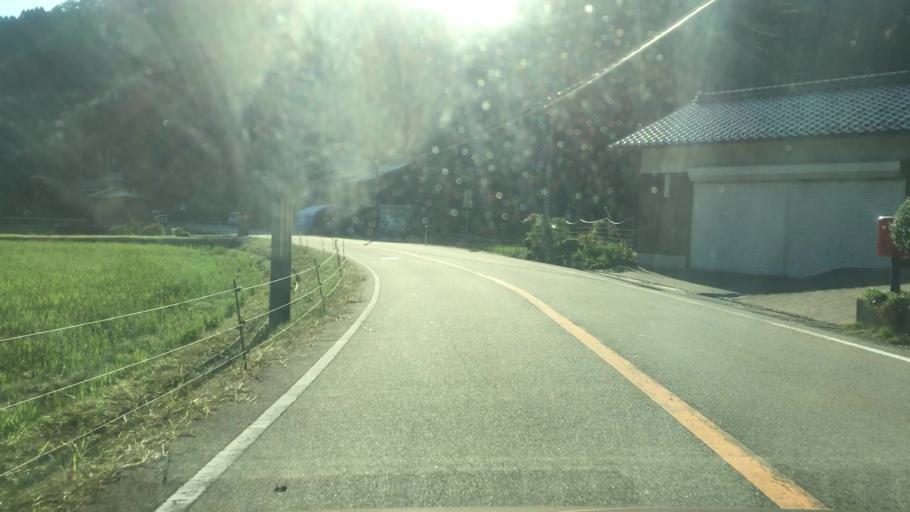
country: JP
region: Hyogo
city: Toyooka
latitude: 35.6216
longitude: 134.8633
